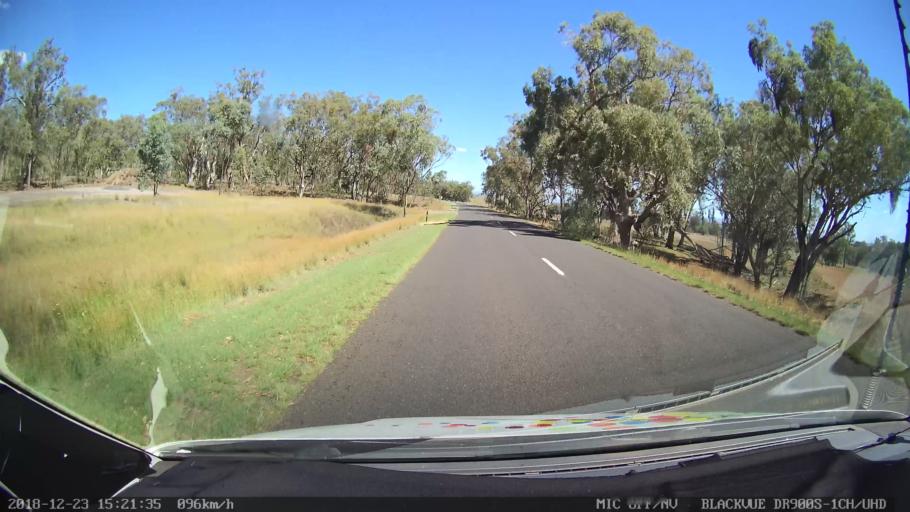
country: AU
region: New South Wales
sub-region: Tamworth Municipality
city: Manilla
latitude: -30.8582
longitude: 150.7975
